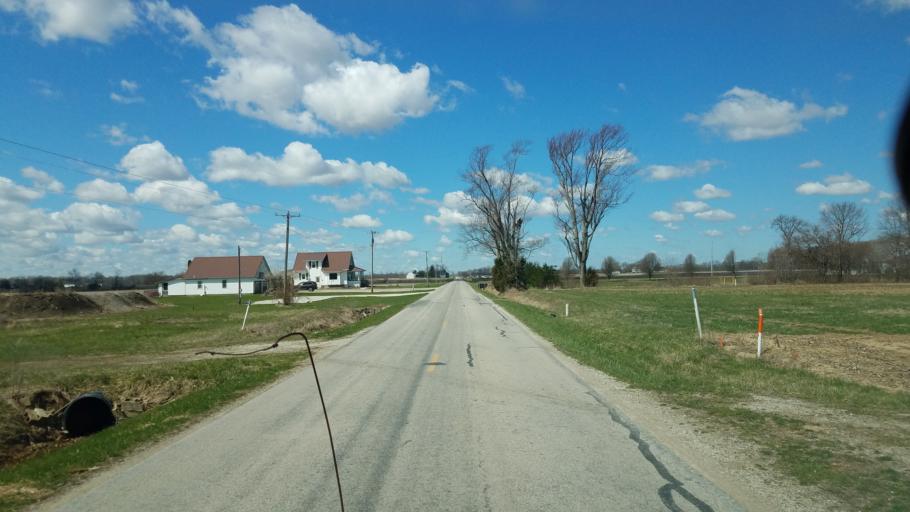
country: US
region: Ohio
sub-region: Sandusky County
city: Green Springs
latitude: 41.2423
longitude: -83.0395
